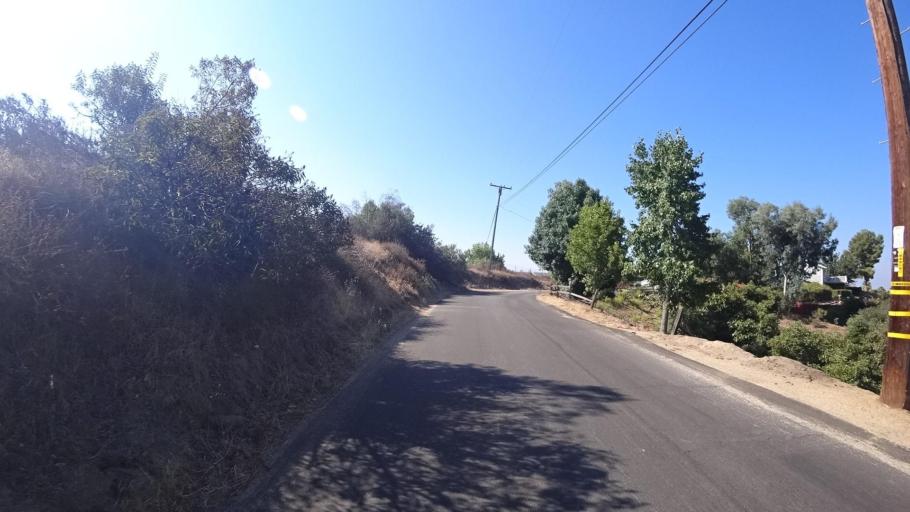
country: US
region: California
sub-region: San Diego County
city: Fallbrook
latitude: 33.3955
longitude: -117.2343
